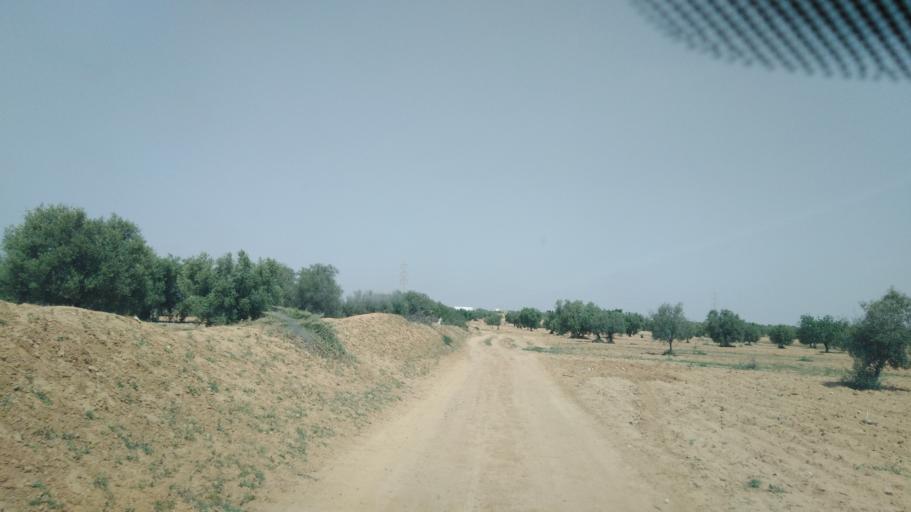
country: TN
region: Safaqis
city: Sfax
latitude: 34.7365
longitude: 10.5737
